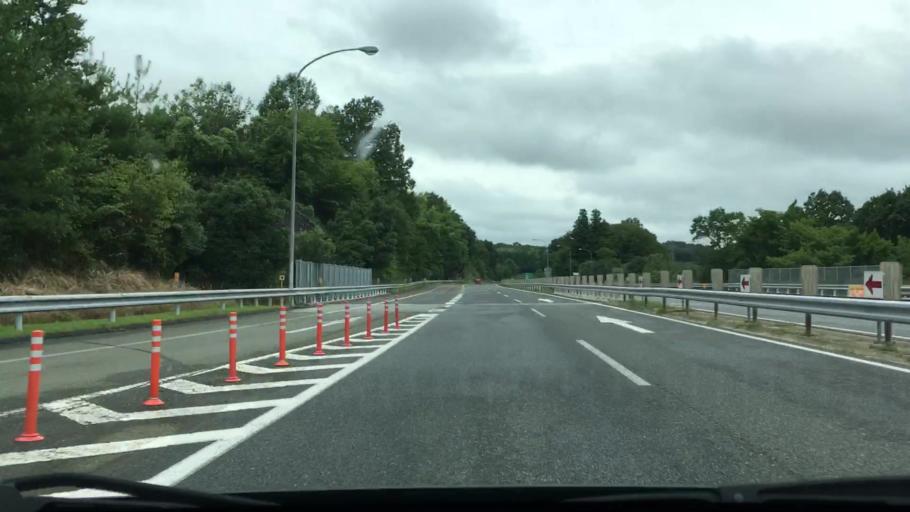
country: JP
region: Hiroshima
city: Shobara
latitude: 34.8456
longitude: 133.0231
